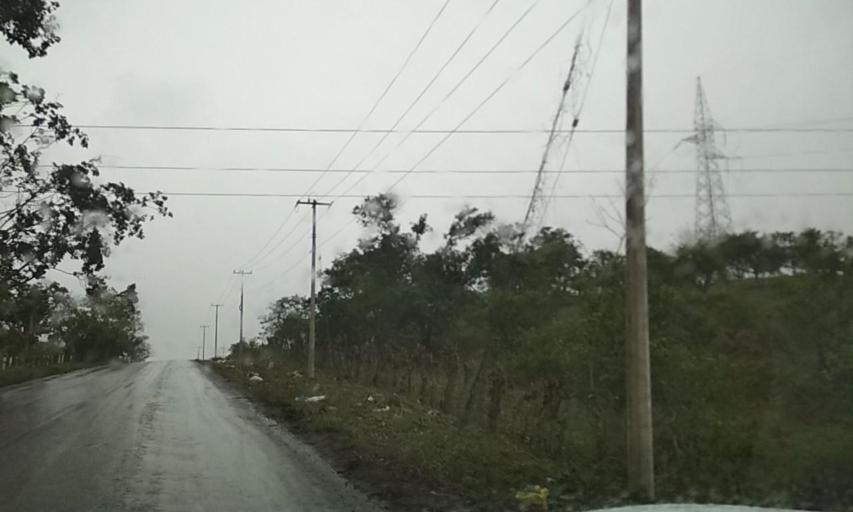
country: MX
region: Veracruz
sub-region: Papantla
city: El Chote
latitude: 20.3950
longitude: -97.3309
